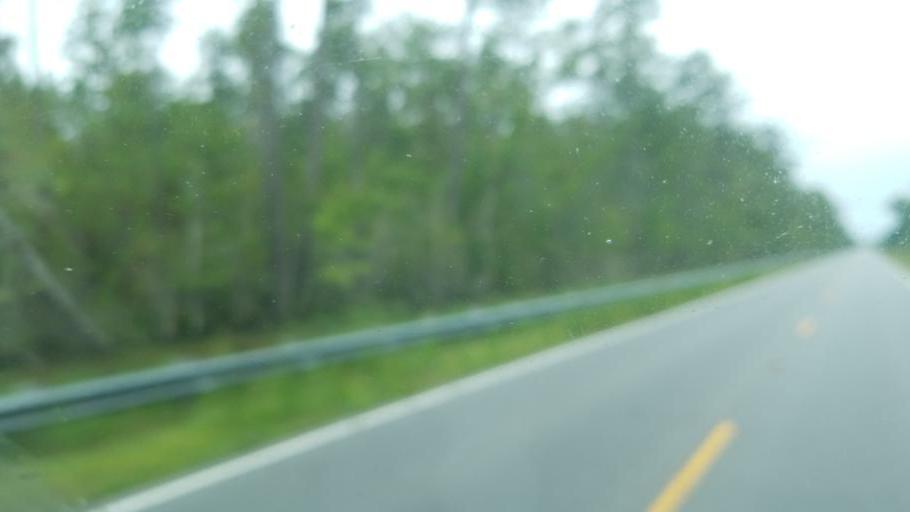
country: US
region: North Carolina
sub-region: Tyrrell County
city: Columbia
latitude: 35.9008
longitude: -76.0815
